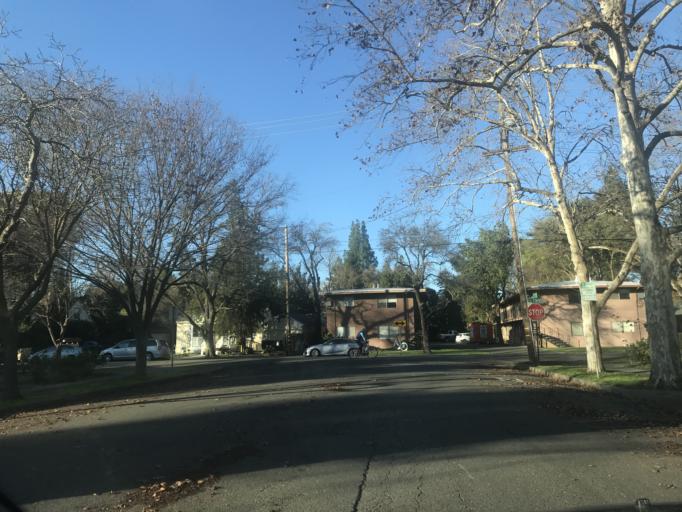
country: US
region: California
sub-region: Yolo County
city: Davis
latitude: 38.5495
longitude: -121.7428
